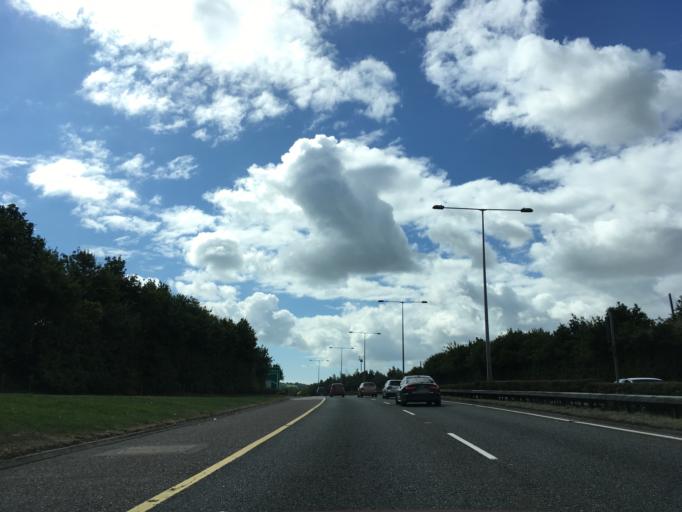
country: IE
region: Munster
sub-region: County Cork
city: Passage West
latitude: 51.8959
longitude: -8.3935
